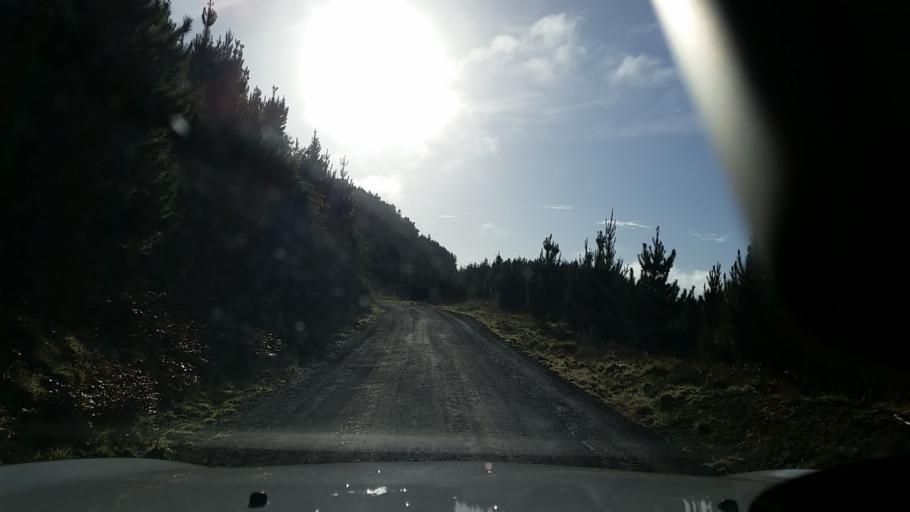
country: NZ
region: Bay of Plenty
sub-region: Kawerau District
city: Kawerau
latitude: -38.0329
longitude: 176.5527
